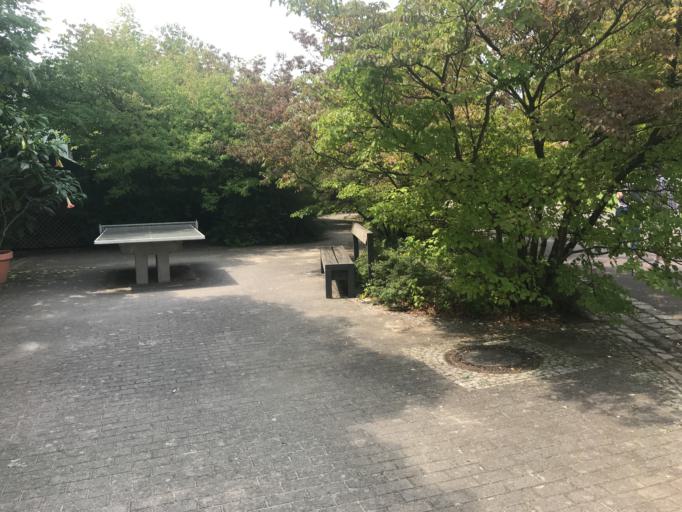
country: DE
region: Berlin
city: Britz
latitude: 52.4321
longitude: 13.4120
